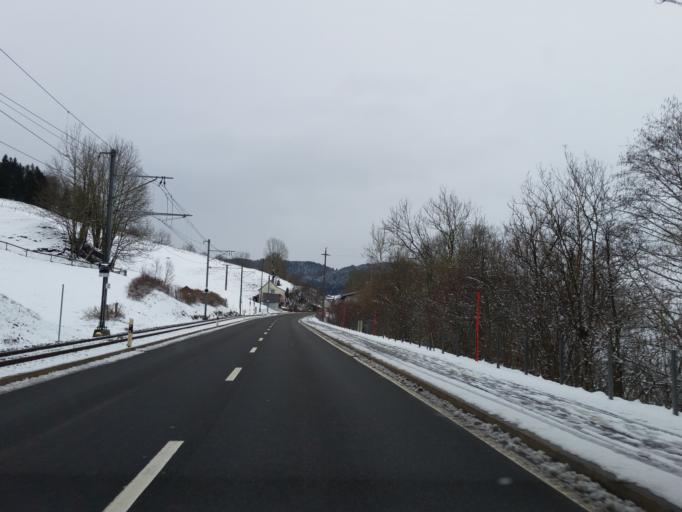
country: CH
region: Appenzell Ausserrhoden
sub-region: Bezirk Mittelland
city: Buhler
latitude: 47.3638
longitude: 9.4338
